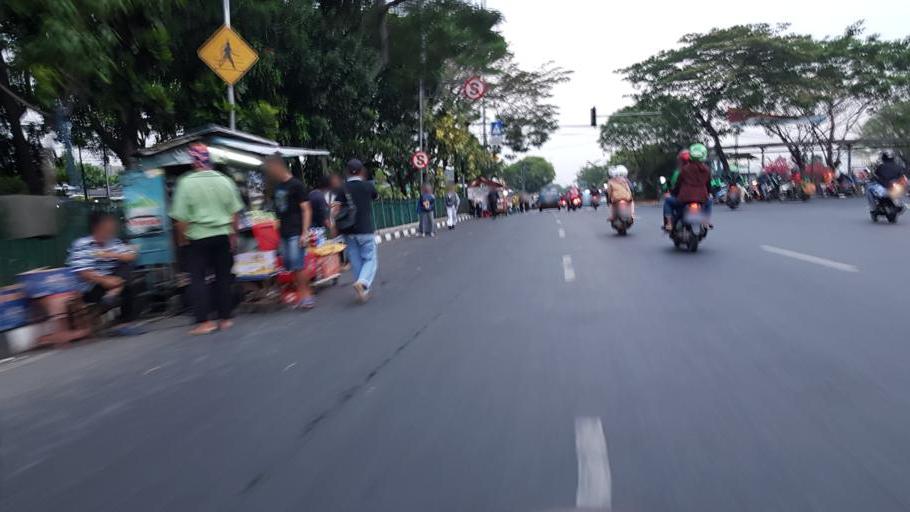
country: ID
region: Jakarta Raya
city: Jakarta
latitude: -6.3081
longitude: 106.8747
